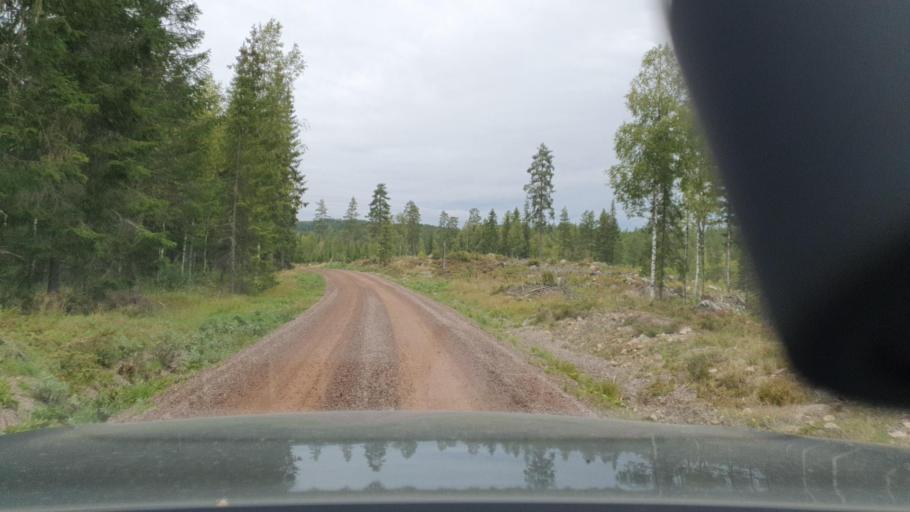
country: SE
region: Vaermland
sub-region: Eda Kommun
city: Charlottenberg
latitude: 60.0447
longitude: 12.5750
